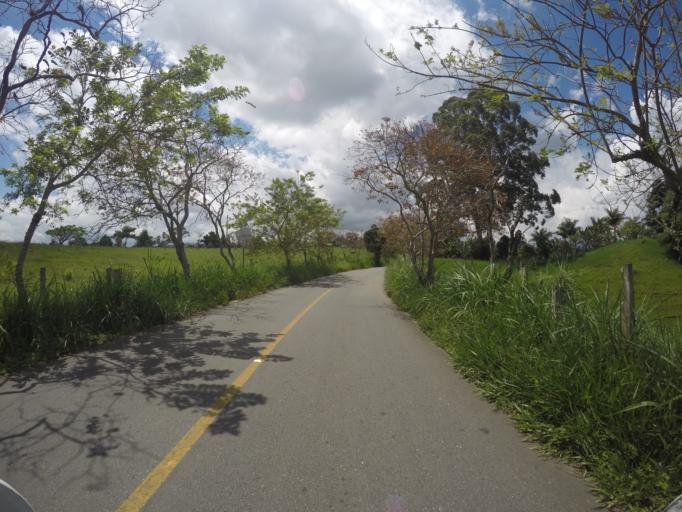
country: CO
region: Quindio
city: Quimbaya
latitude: 4.6308
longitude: -75.7142
